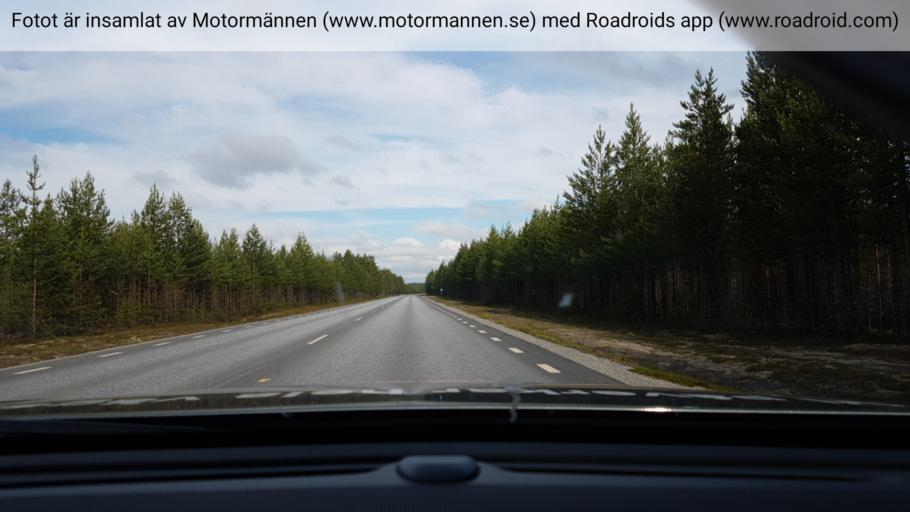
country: SE
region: Vaesterbotten
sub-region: Vindelns Kommun
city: Vindeln
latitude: 64.1609
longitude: 19.8268
